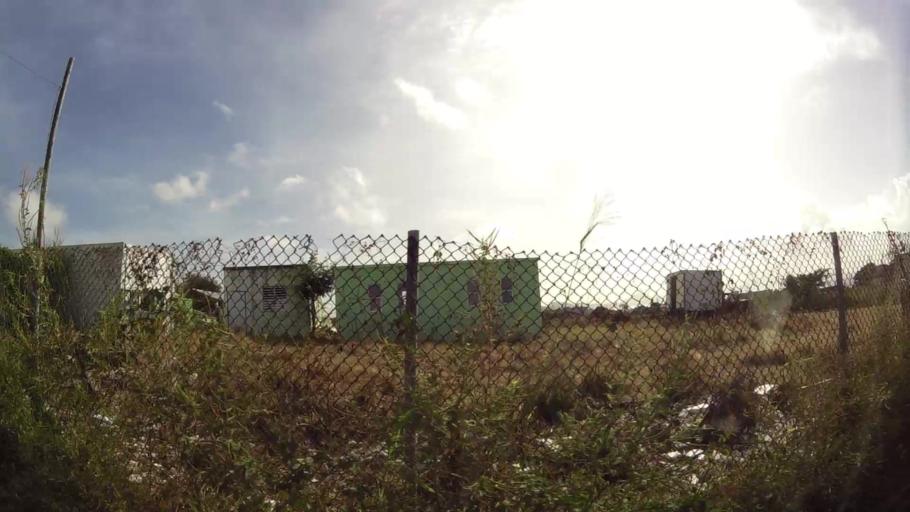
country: KN
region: Saint George Basseterre
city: Basseterre
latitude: 17.2941
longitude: -62.7395
